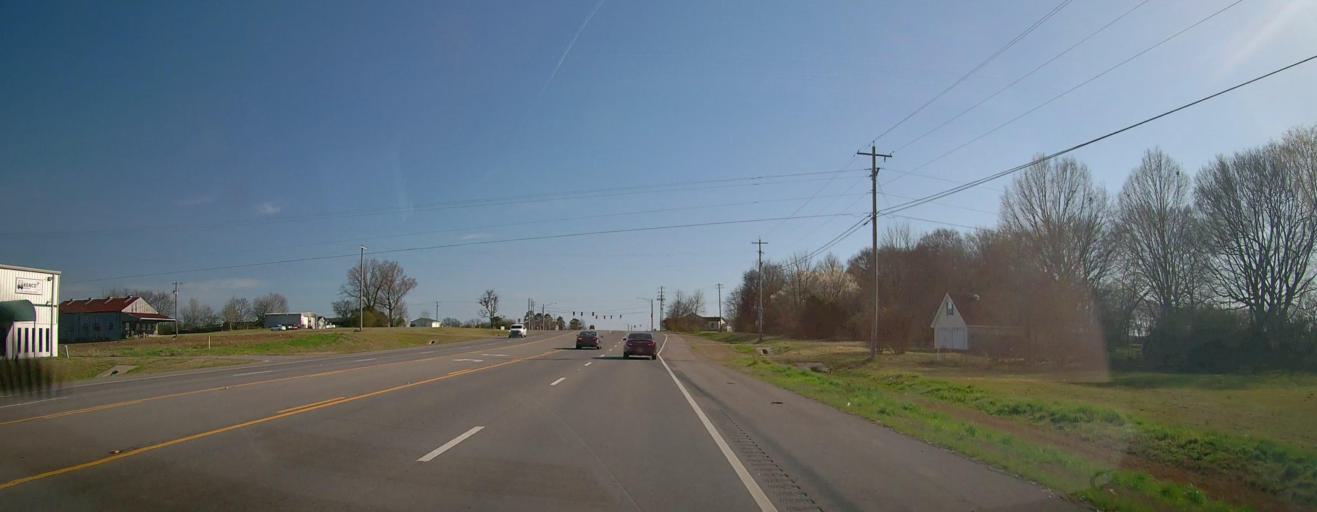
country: US
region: Alabama
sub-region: Colbert County
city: Muscle Shoals
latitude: 34.7033
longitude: -87.6348
